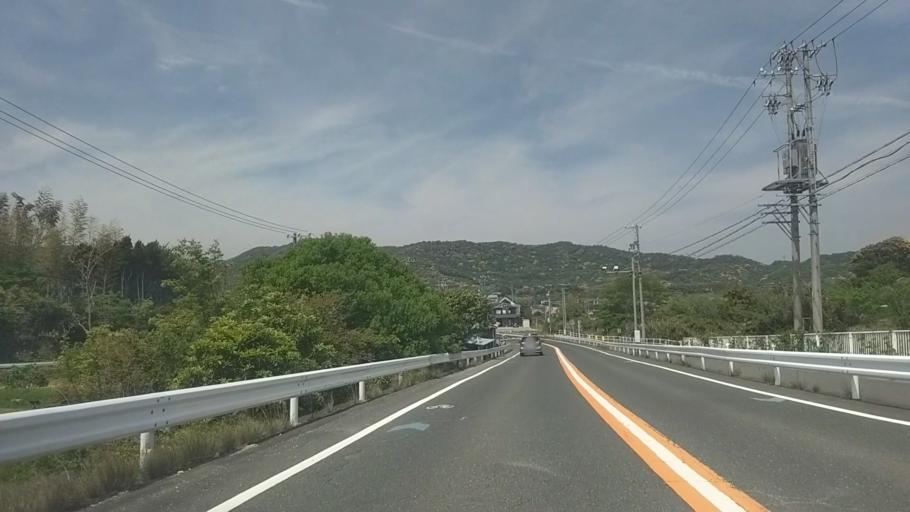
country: JP
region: Shizuoka
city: Kosai-shi
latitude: 34.7506
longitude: 137.5115
